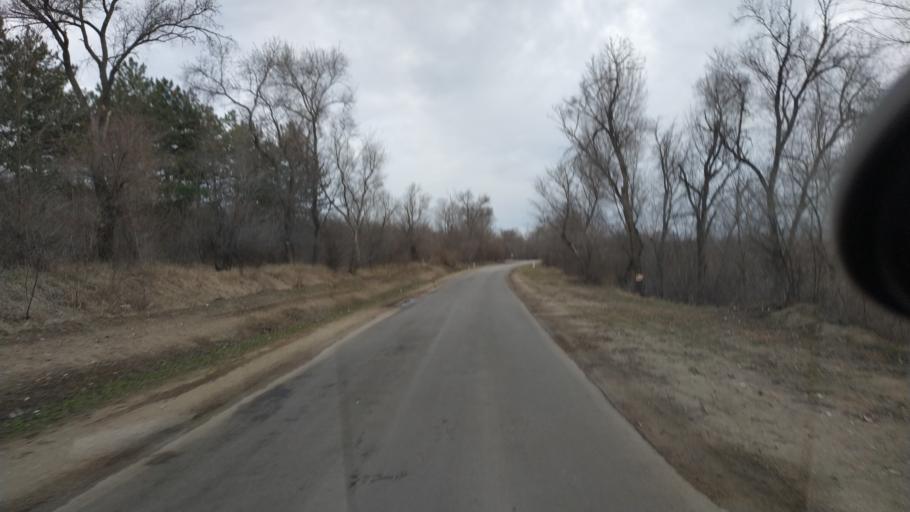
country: MD
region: Criuleni
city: Criuleni
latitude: 47.2308
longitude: 29.1584
